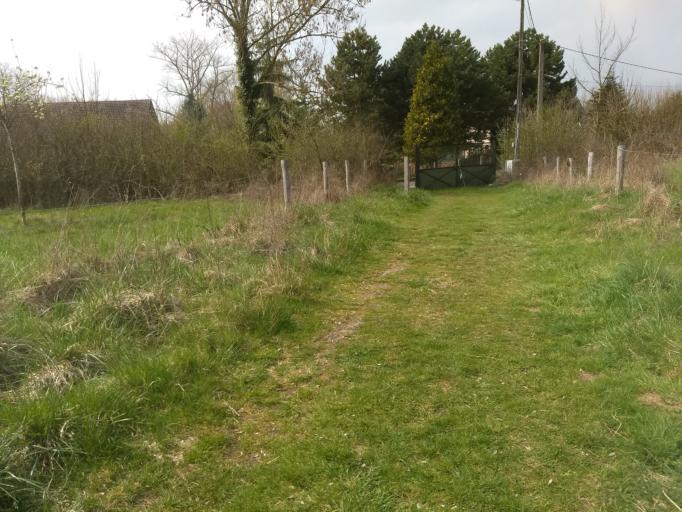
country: FR
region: Nord-Pas-de-Calais
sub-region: Departement du Pas-de-Calais
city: Mont-Saint-Eloi
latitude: 50.3355
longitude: 2.6913
